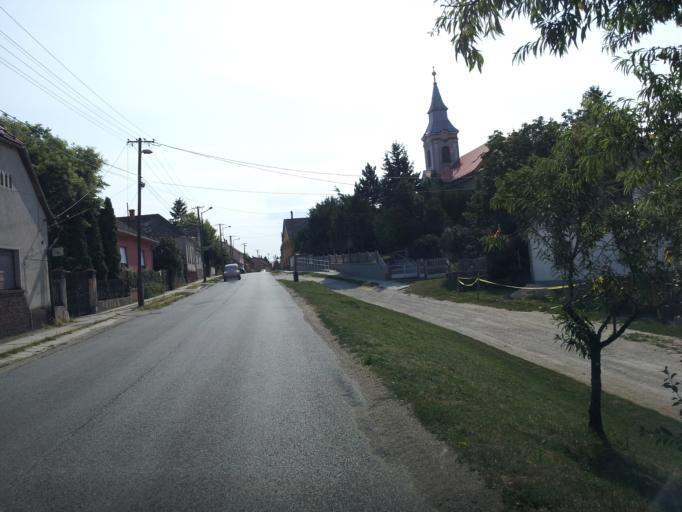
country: HU
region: Veszprem
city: Balatonkenese
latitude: 47.0829
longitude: 18.0839
